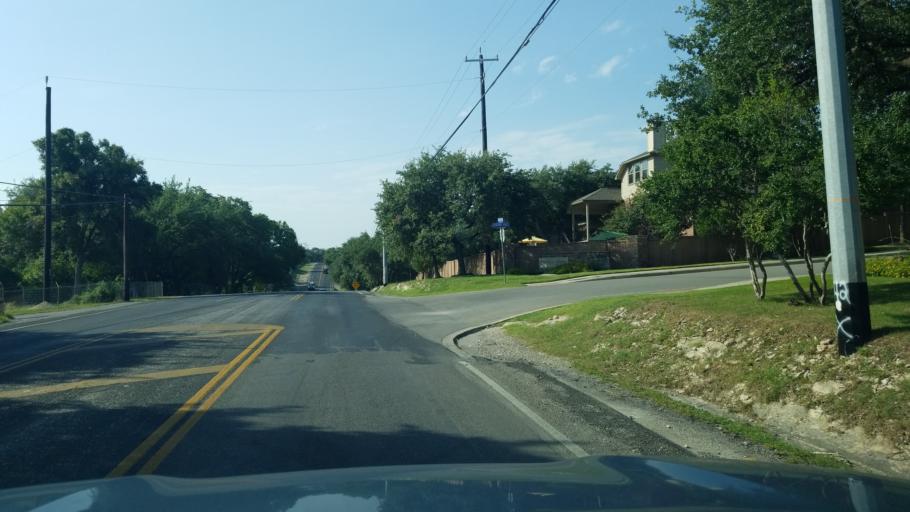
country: US
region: Texas
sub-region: Bexar County
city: Leon Valley
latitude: 29.4415
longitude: -98.7502
